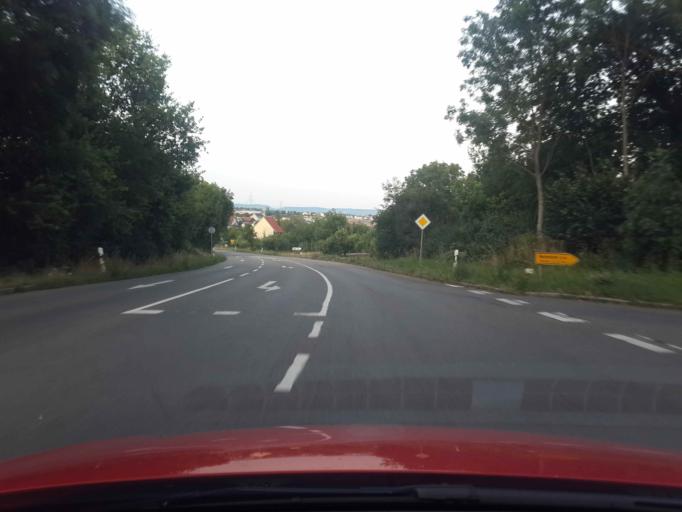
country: DE
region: Baden-Wuerttemberg
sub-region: Regierungsbezirk Stuttgart
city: Nordheim
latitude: 49.0992
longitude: 9.1018
